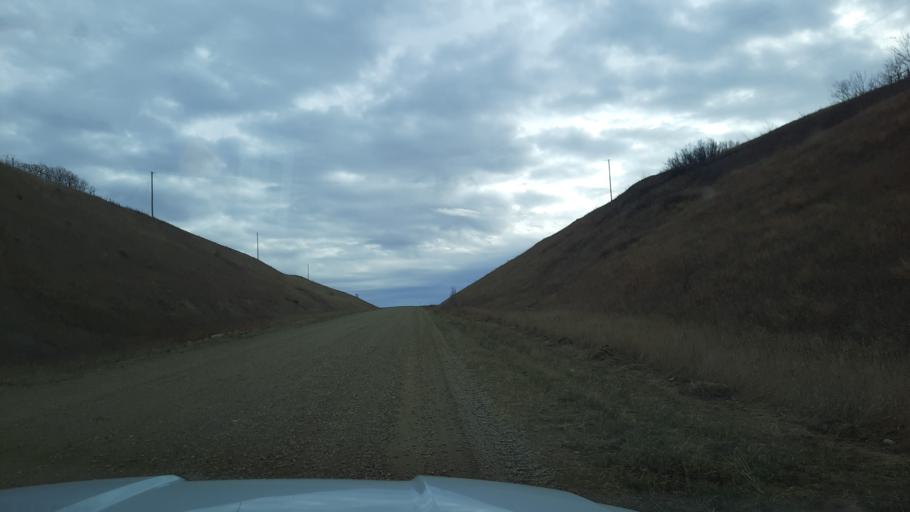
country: CA
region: Saskatchewan
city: Pilot Butte
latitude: 50.7670
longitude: -104.2775
